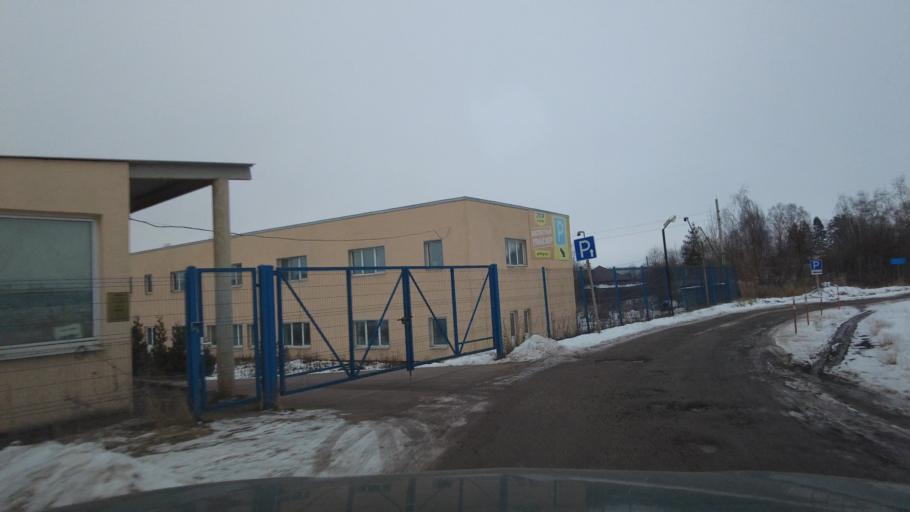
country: RU
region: Moskovskaya
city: Novopodrezkovo
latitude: 55.9754
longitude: 37.3818
